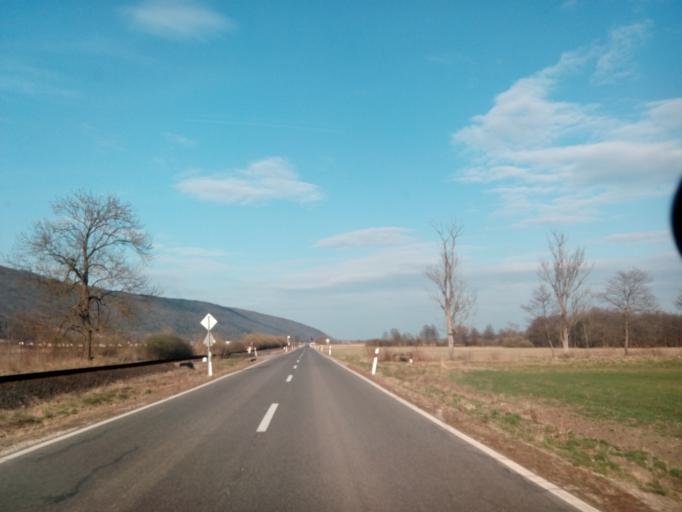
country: HU
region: Borsod-Abauj-Zemplen
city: Szendro
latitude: 48.5507
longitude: 20.7685
